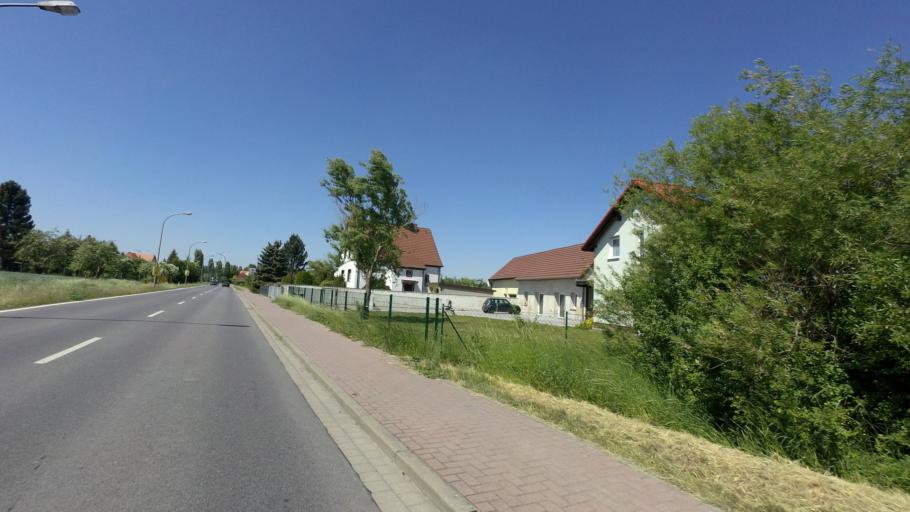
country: DE
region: Brandenburg
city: Drehnow
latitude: 51.8678
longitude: 14.3854
